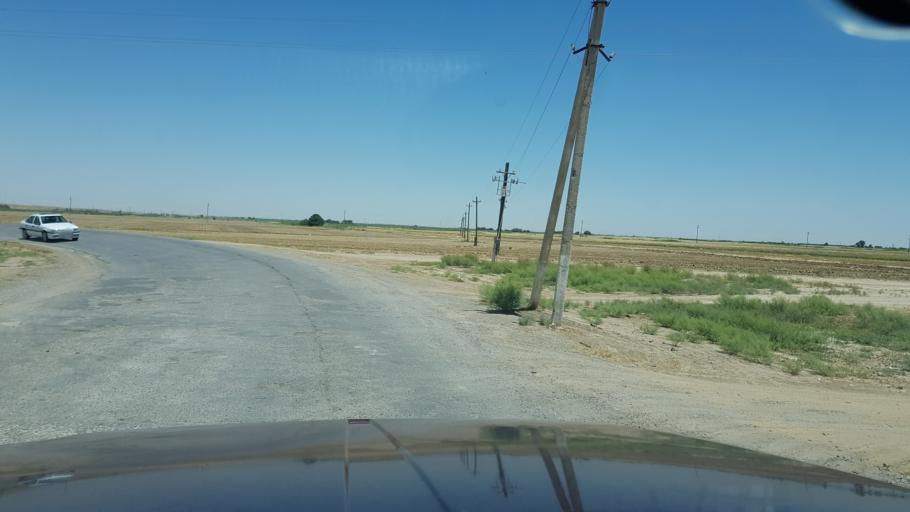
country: TM
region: Ahal
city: Annau
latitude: 37.8486
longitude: 58.7143
